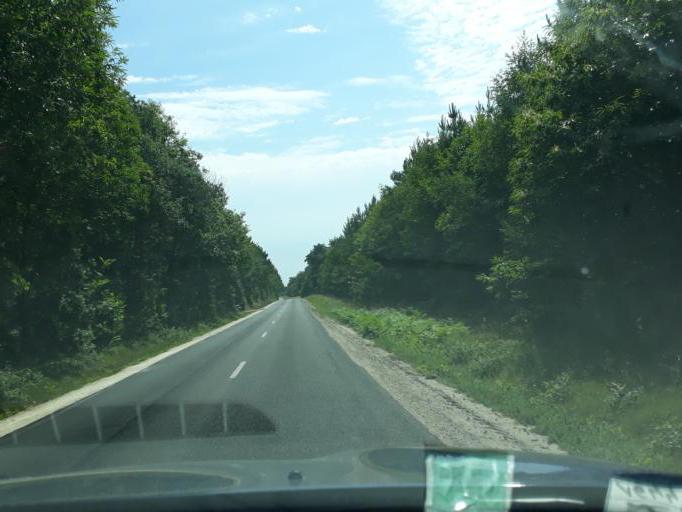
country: FR
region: Centre
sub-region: Departement du Loir-et-Cher
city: Vouzon
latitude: 47.6462
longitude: 2.0383
